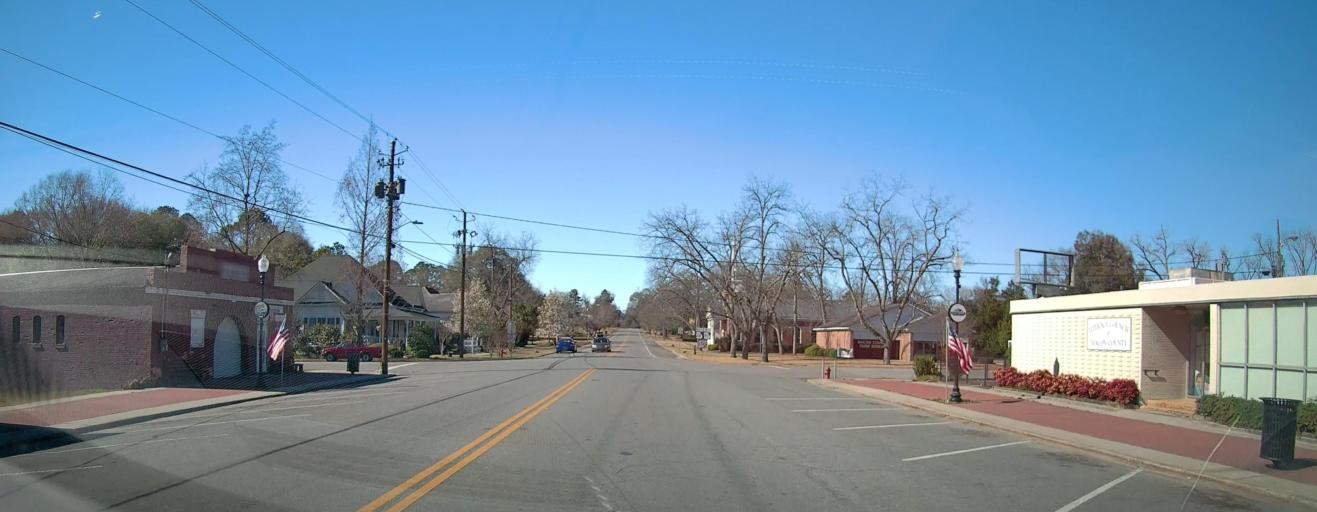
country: US
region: Georgia
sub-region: Macon County
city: Oglethorpe
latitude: 32.2944
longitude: -84.0613
